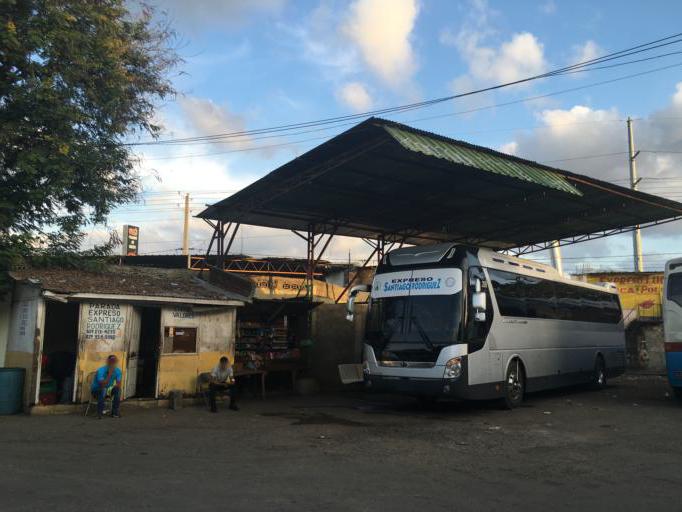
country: DO
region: Santiago
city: Santiago de los Caballeros
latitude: 19.4880
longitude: -70.7178
